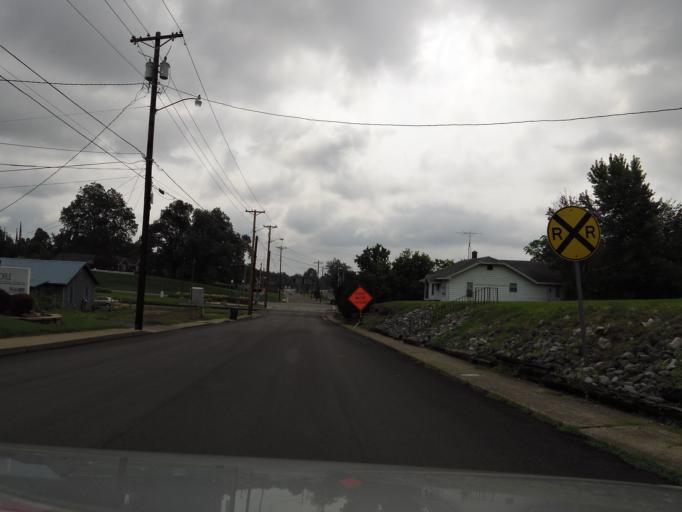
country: US
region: Kentucky
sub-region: Hopkins County
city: Madisonville
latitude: 37.3356
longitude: -87.4990
